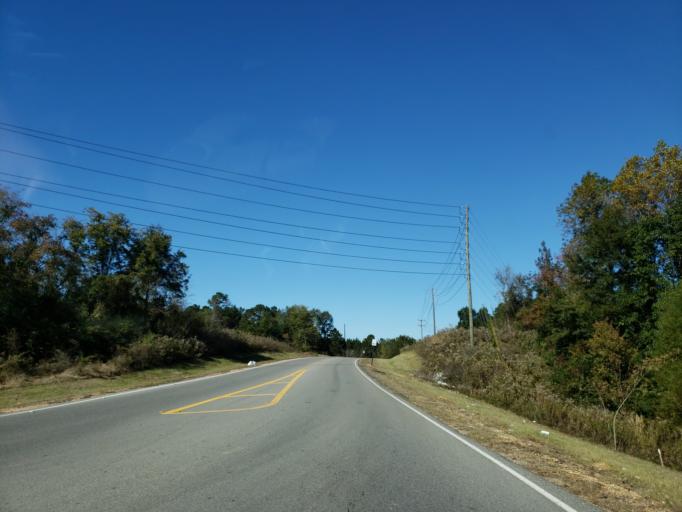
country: US
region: Mississippi
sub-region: Lamar County
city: West Hattiesburg
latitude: 31.3254
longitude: -89.3996
